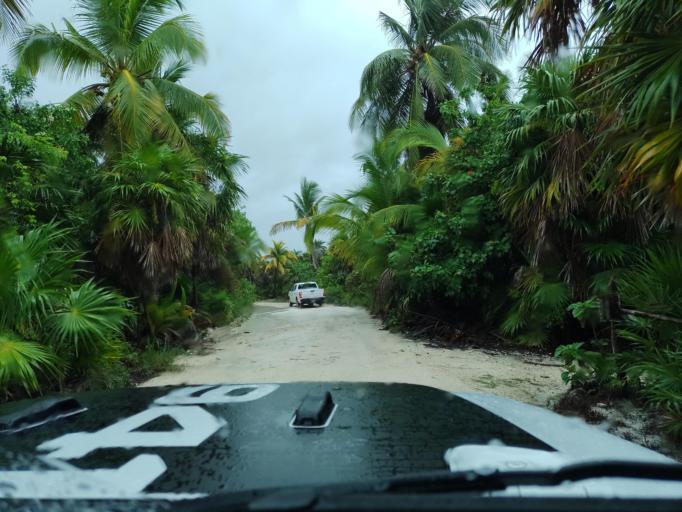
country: MX
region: Quintana Roo
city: Tulum
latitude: 19.9825
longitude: -87.4681
